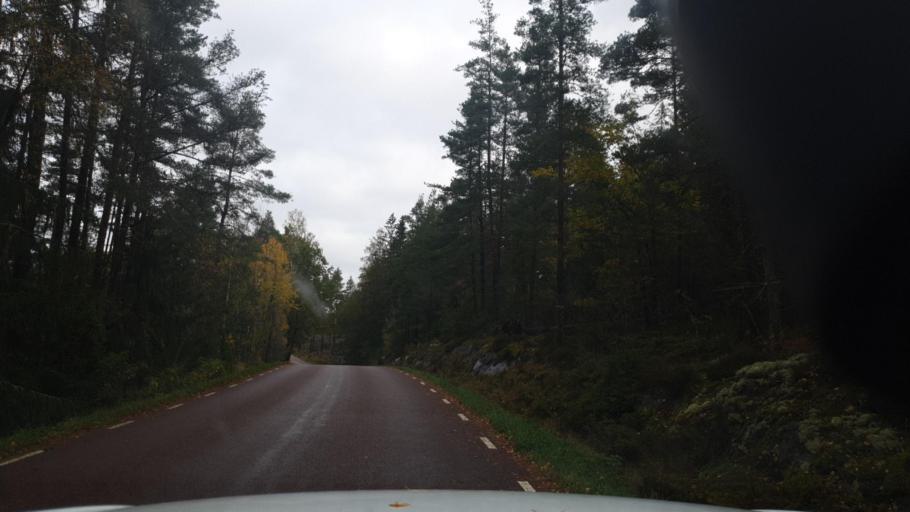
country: SE
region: Vaermland
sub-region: Grums Kommun
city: Grums
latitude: 59.4199
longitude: 13.0865
